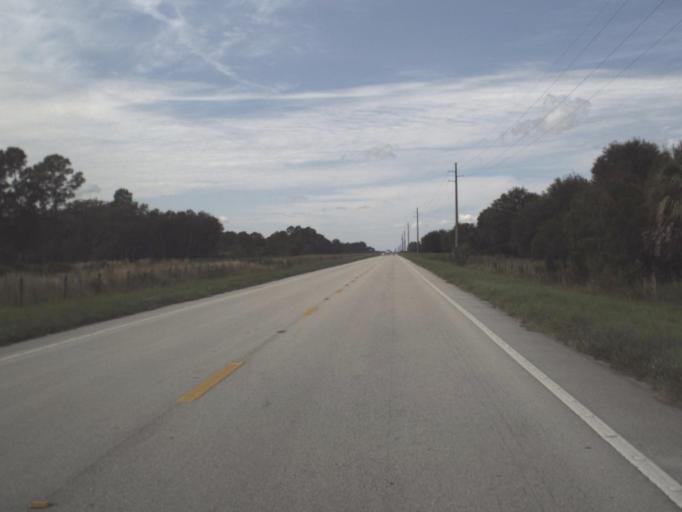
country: US
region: Florida
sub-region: Highlands County
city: Placid Lakes
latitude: 27.2088
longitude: -81.4831
